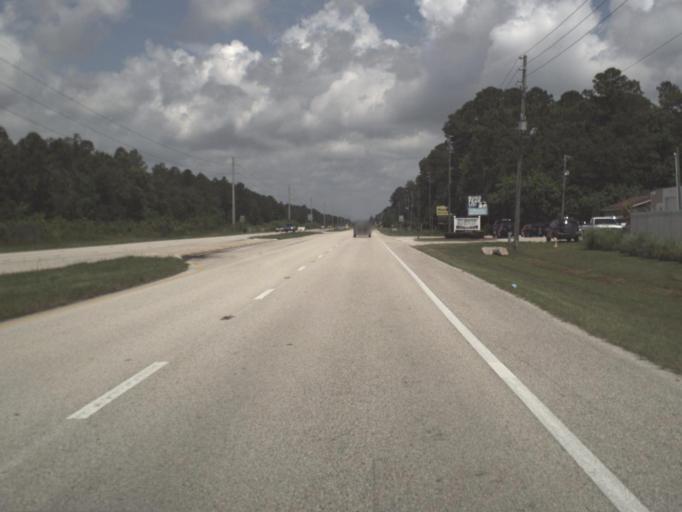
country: US
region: Florida
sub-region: Saint Johns County
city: Villano Beach
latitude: 29.9820
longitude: -81.3645
